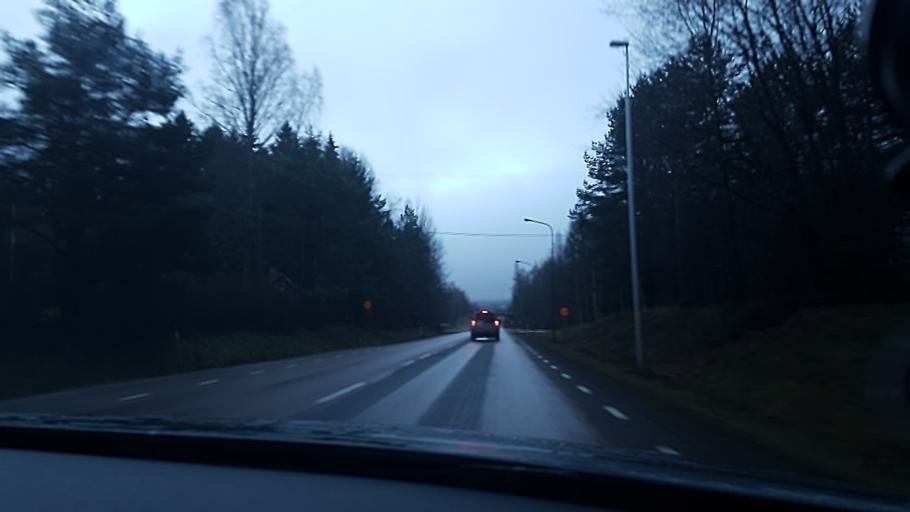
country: SE
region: Vaermland
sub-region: Kristinehamns Kommun
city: Kristinehamn
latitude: 59.3278
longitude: 14.1169
